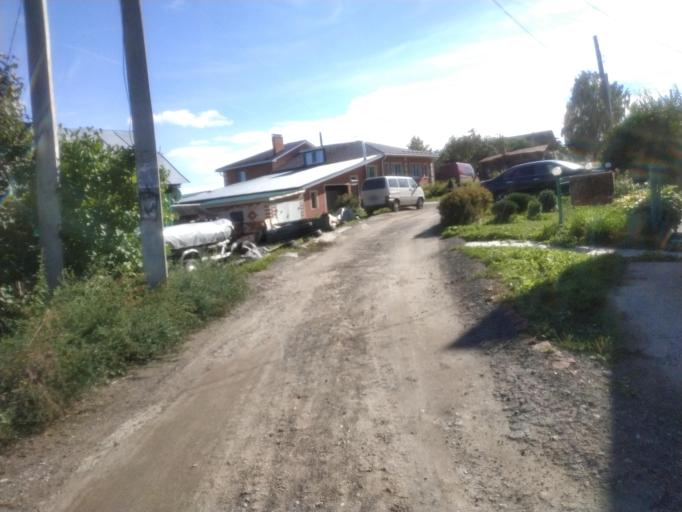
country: RU
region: Chuvashia
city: Novyye Lapsary
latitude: 56.1452
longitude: 47.1500
